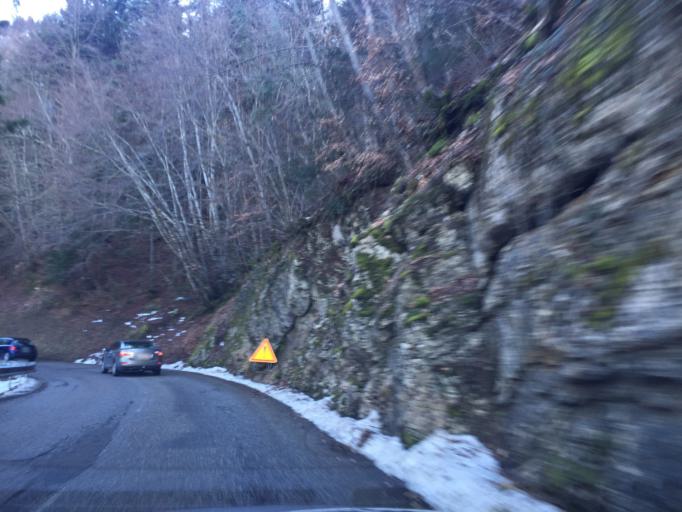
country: FR
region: Rhone-Alpes
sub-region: Departement de la Haute-Savoie
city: Cusy
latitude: 45.7029
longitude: 6.0022
